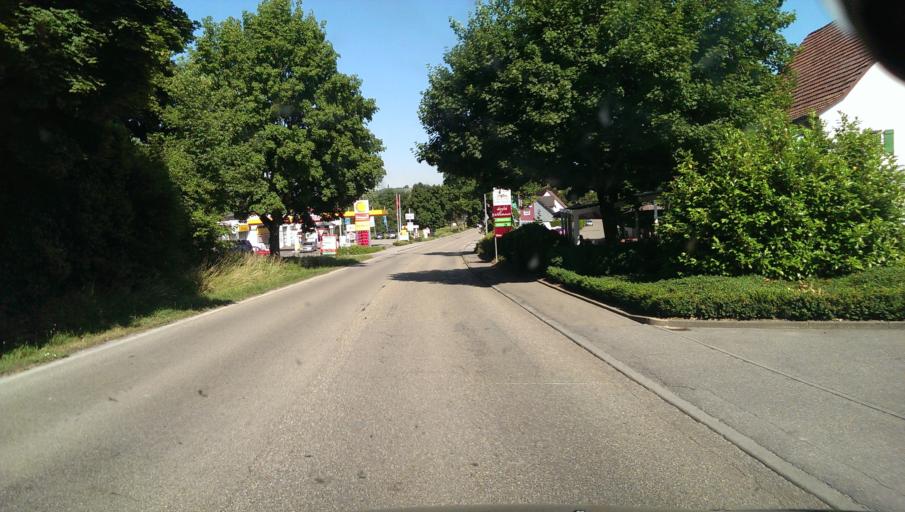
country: DE
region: Baden-Wuerttemberg
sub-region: Regierungsbezirk Stuttgart
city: Bretzfeld
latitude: 49.1898
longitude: 9.4402
